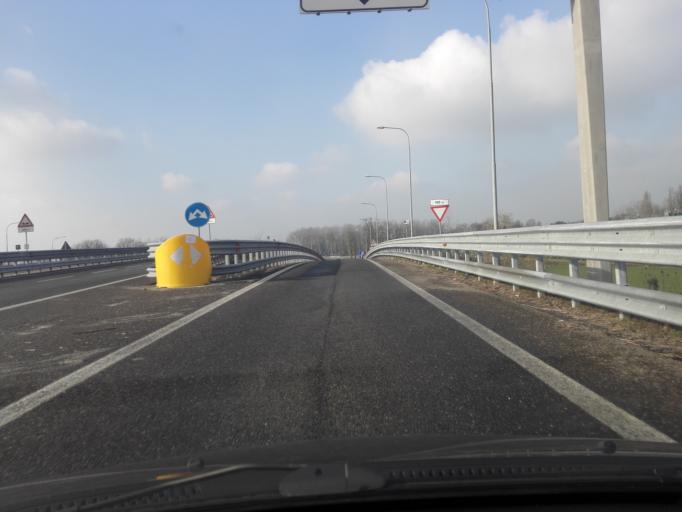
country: IT
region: Piedmont
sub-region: Provincia di Alessandria
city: Valle San Bartolomeo
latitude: 44.9336
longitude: 8.6284
